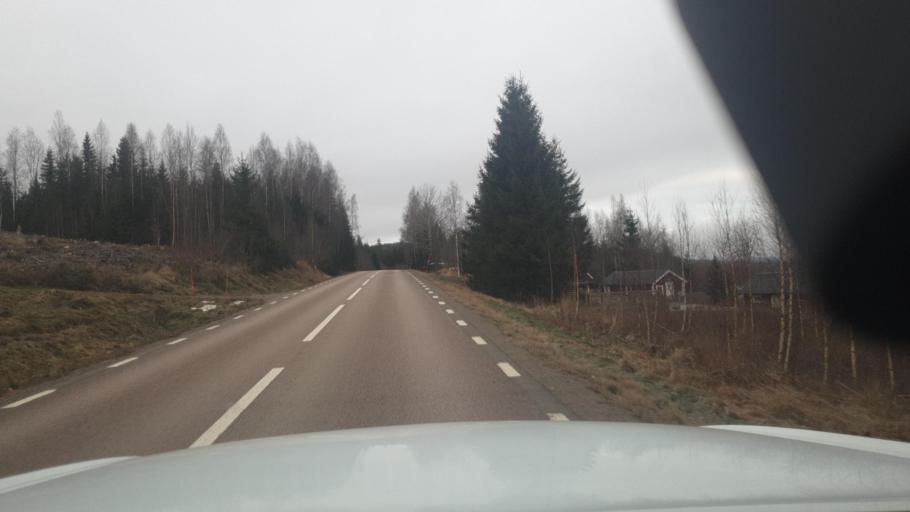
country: SE
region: Vaermland
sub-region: Sunne Kommun
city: Sunne
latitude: 59.9011
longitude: 12.9109
